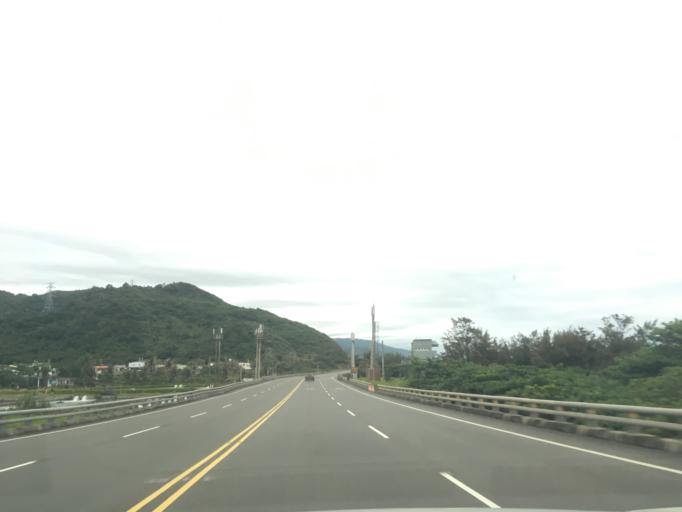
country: TW
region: Taiwan
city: Hengchun
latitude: 22.3059
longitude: 120.8899
